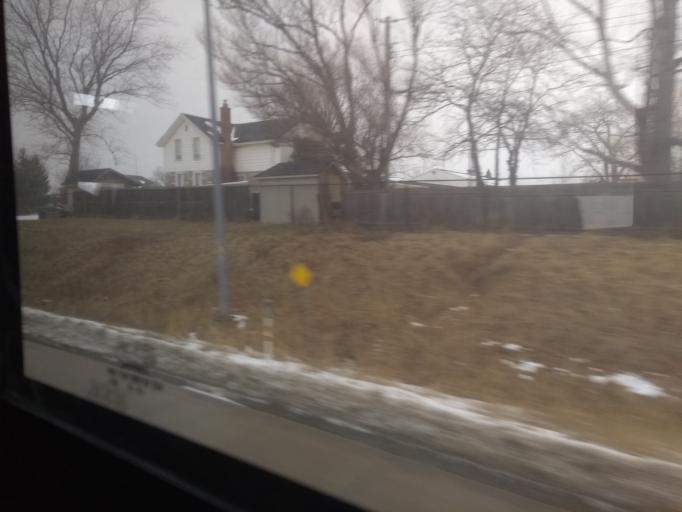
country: CA
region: Ontario
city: Welland
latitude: 42.9936
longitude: -79.2091
